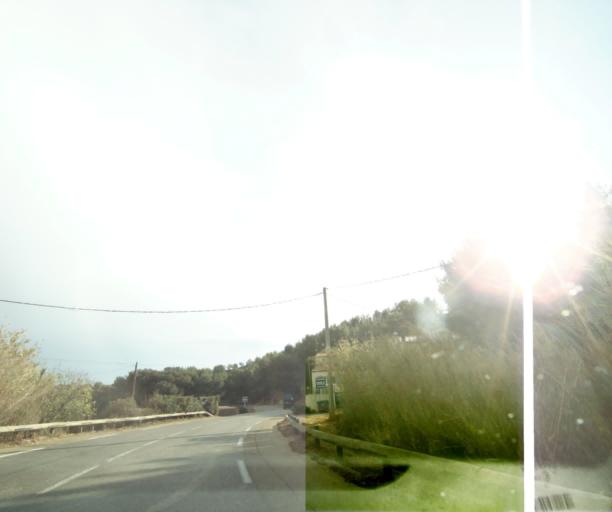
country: FR
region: Provence-Alpes-Cote d'Azur
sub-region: Departement des Bouches-du-Rhone
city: Sausset-les-Pins
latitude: 43.3449
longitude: 5.1037
